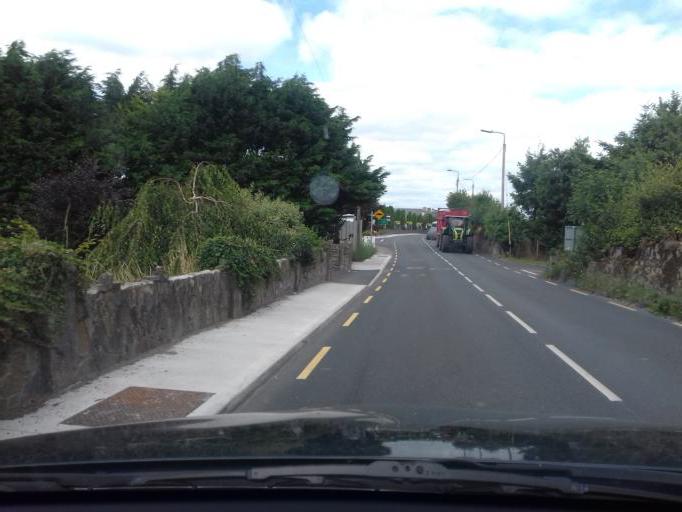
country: IE
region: Leinster
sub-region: County Carlow
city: Tullow
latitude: 52.7947
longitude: -6.7489
